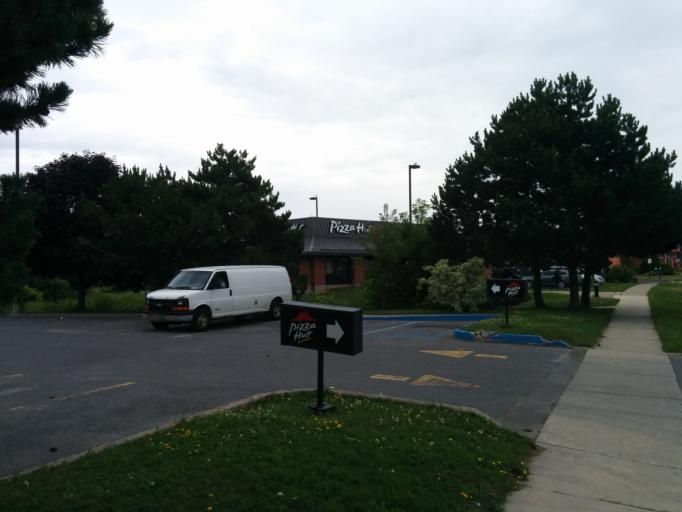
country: CA
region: Ontario
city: Kingston
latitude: 44.2669
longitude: -76.5013
